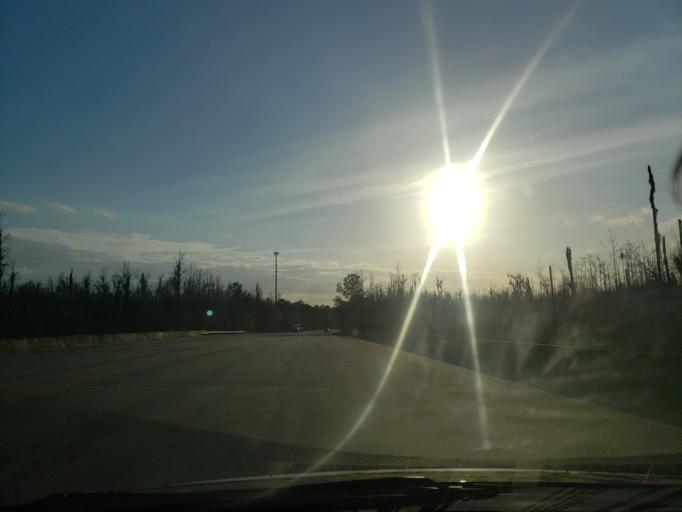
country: US
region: Georgia
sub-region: Chatham County
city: Bloomingdale
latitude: 32.1528
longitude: -81.2793
